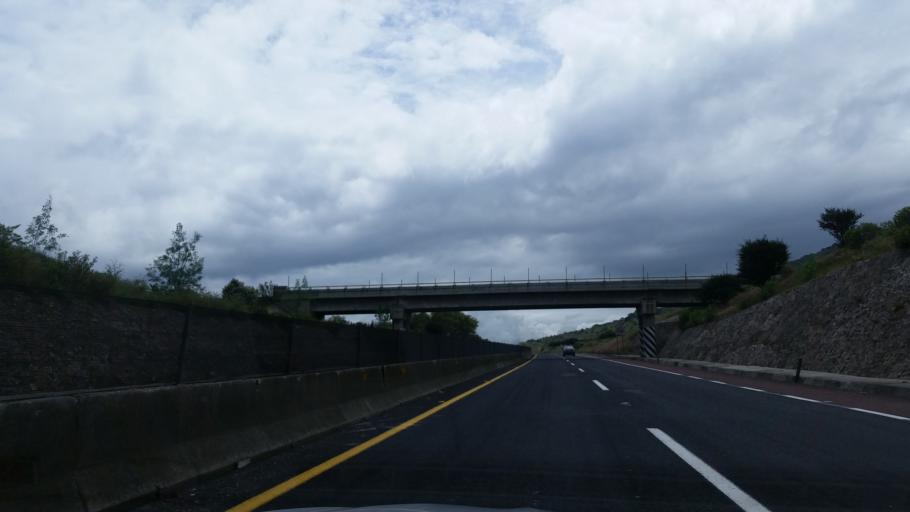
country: MX
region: Mexico
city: San Francisco Soyaniquilpan
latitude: 20.0318
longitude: -99.4558
